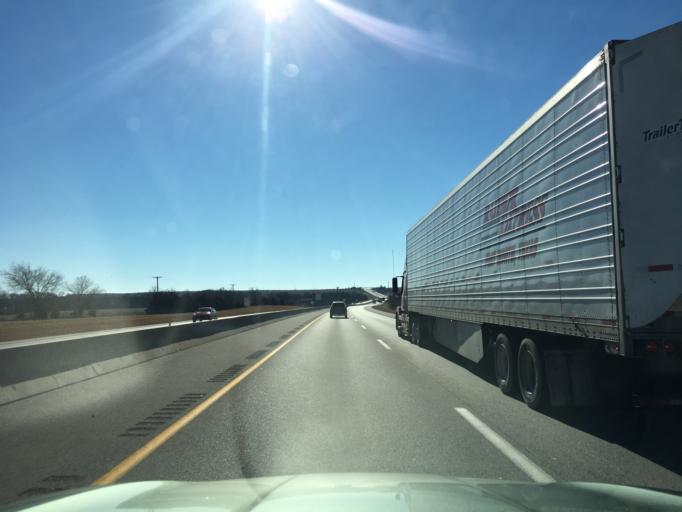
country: US
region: Kansas
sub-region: Sumner County
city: Wellington
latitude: 37.2227
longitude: -97.3388
